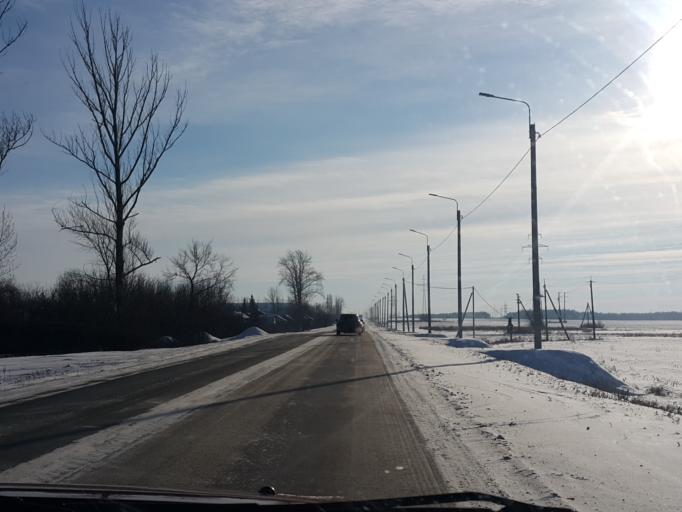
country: RU
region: Tambov
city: Znamenka
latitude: 52.4338
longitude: 41.4969
